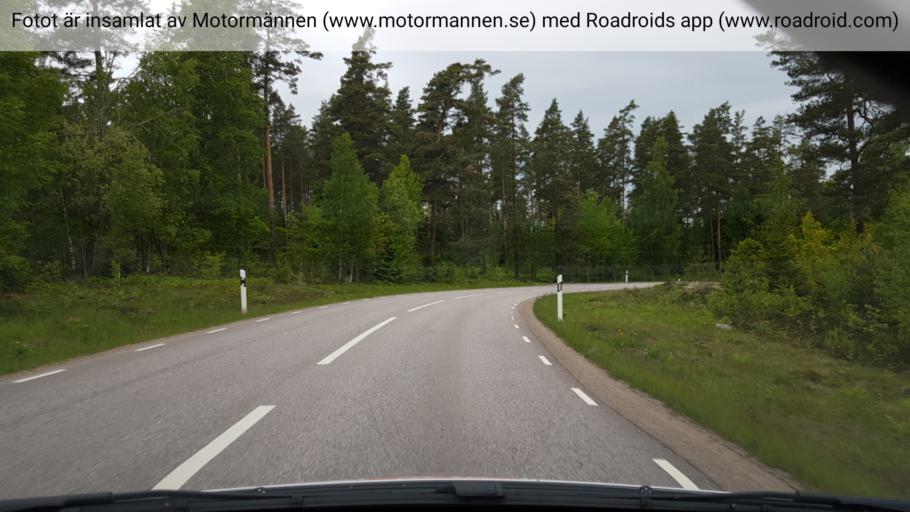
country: SE
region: OEstergoetland
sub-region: Motala Kommun
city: Borensberg
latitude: 58.5838
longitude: 15.2711
